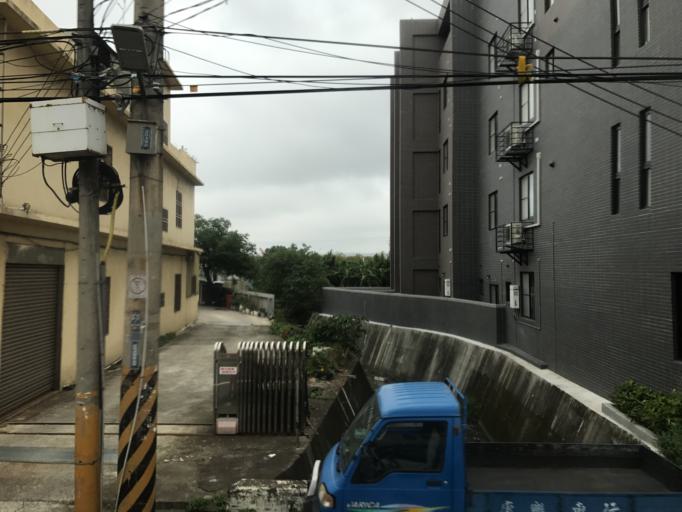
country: TW
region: Taiwan
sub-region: Hsinchu
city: Hsinchu
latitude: 24.8367
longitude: 120.9432
